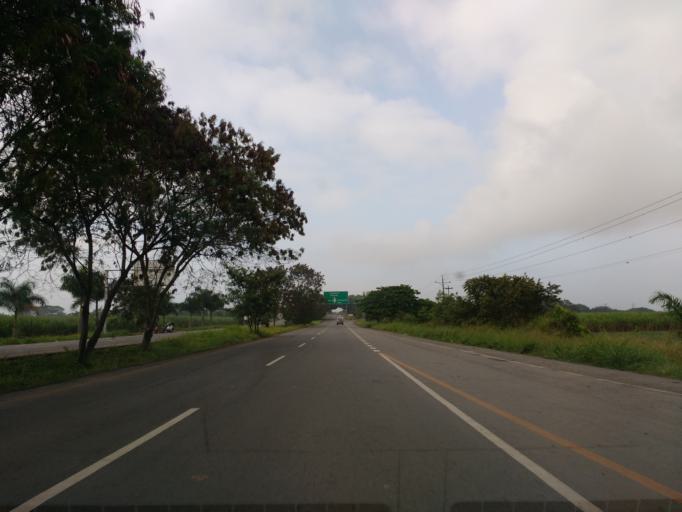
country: CO
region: Valle del Cauca
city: Palmira
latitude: 3.5292
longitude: -76.3376
